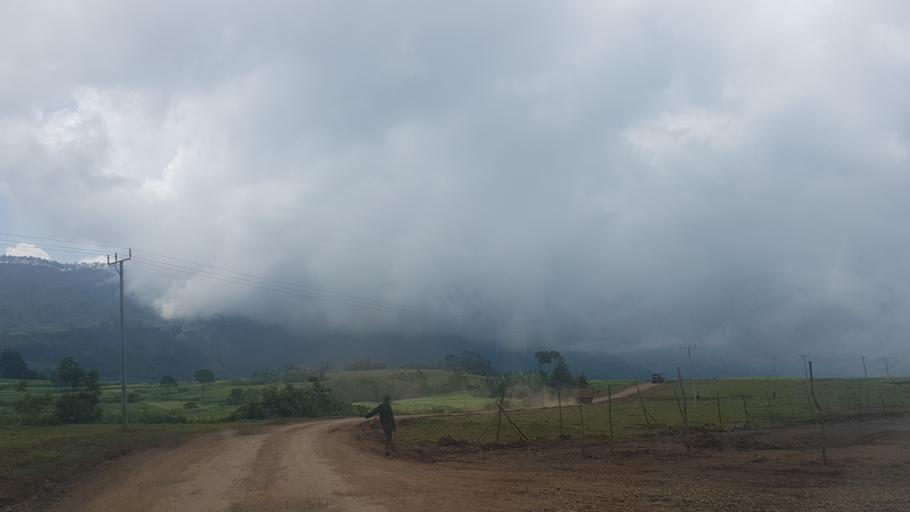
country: ET
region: Southern Nations, Nationalities, and People's Region
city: Arba Minch'
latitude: 6.3250
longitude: 37.5421
